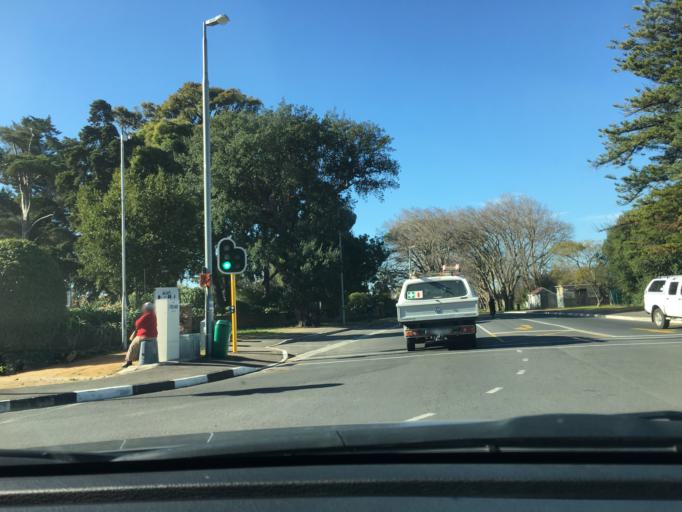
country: ZA
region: Western Cape
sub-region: City of Cape Town
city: Constantia
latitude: -34.0216
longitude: 18.4385
